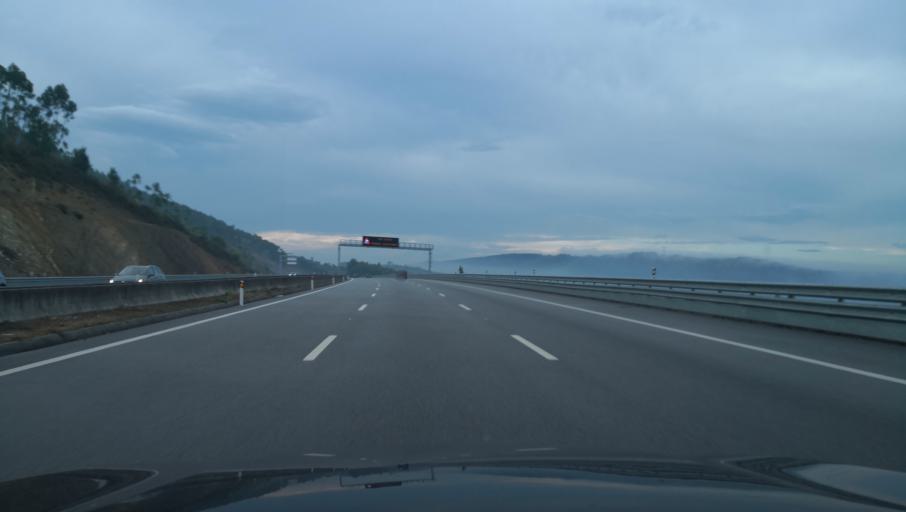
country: PT
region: Porto
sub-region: Paredes
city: Recarei
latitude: 41.1193
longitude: -8.4335
